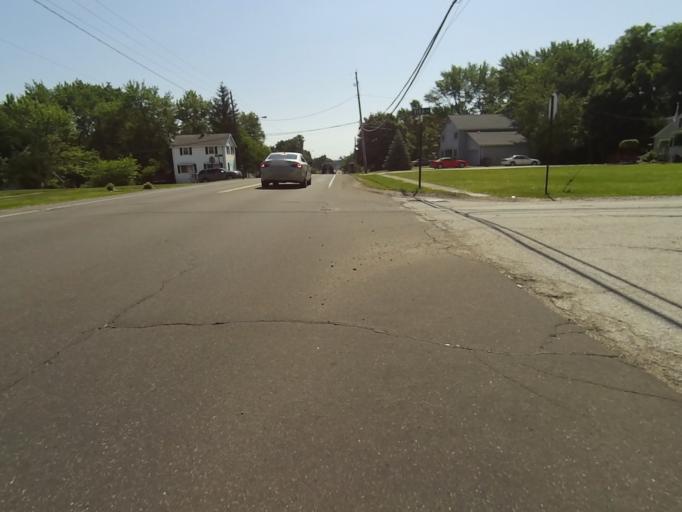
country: US
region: Ohio
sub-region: Summit County
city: Stow
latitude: 41.1667
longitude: -81.4204
